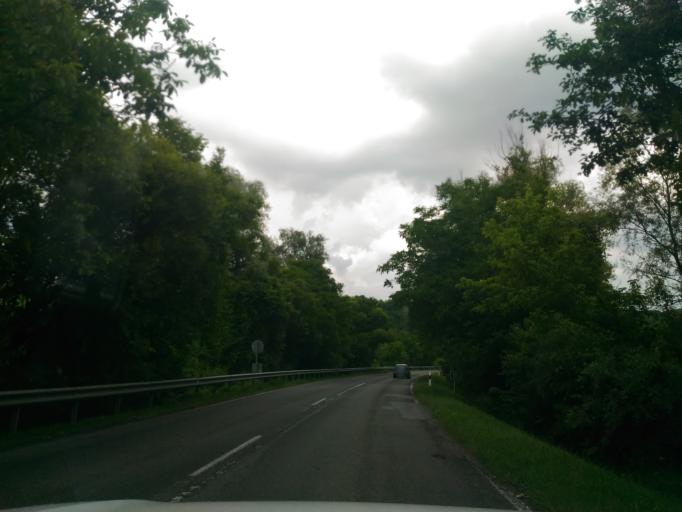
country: HU
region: Baranya
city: Hidas
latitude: 46.2463
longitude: 18.4787
